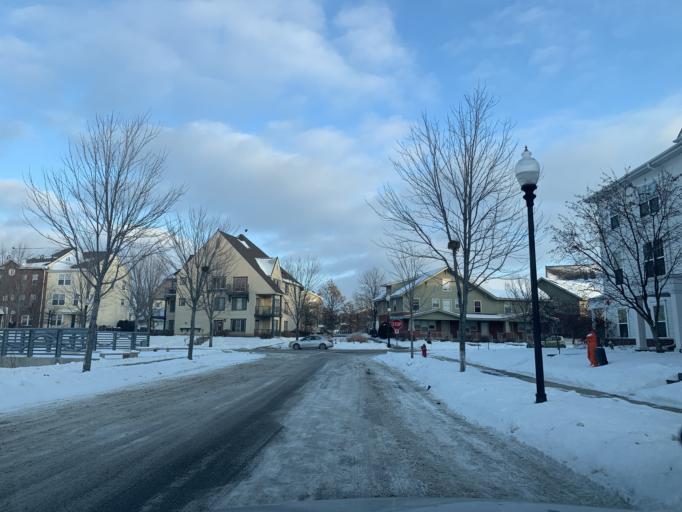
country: US
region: Minnesota
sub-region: Hennepin County
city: Minneapolis
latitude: 44.9863
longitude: -93.2917
